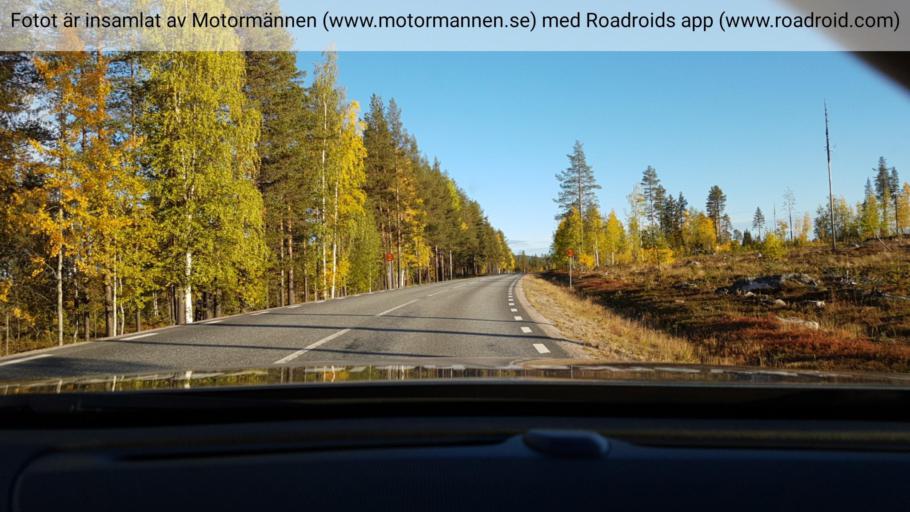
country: SE
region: Norrbotten
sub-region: Jokkmokks Kommun
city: Jokkmokk
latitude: 66.7992
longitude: 19.8748
